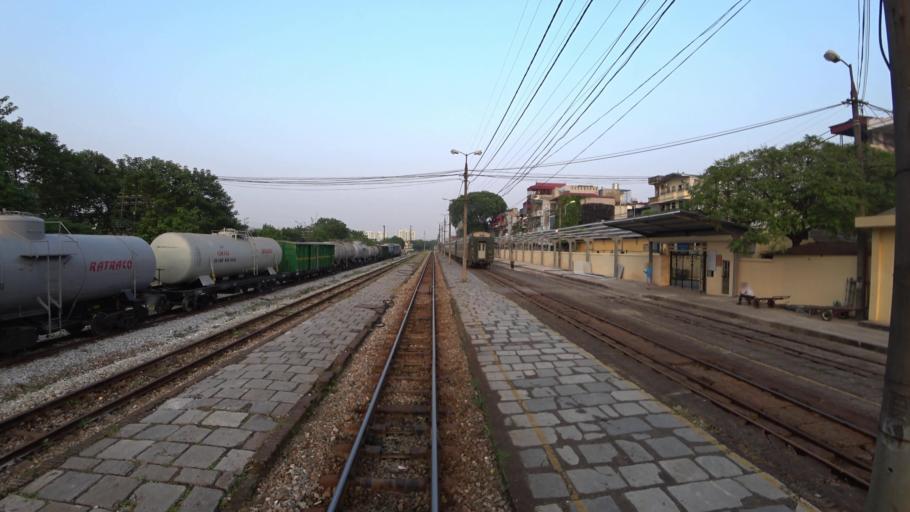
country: VN
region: Ha Noi
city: Hoan Kiem
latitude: 21.0575
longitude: 105.8891
